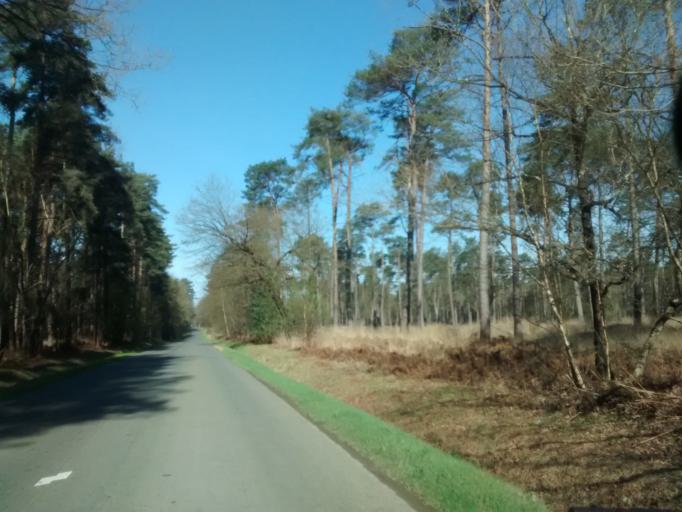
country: FR
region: Brittany
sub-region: Departement d'Ille-et-Vilaine
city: Liffre
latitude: 48.2048
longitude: -1.5365
